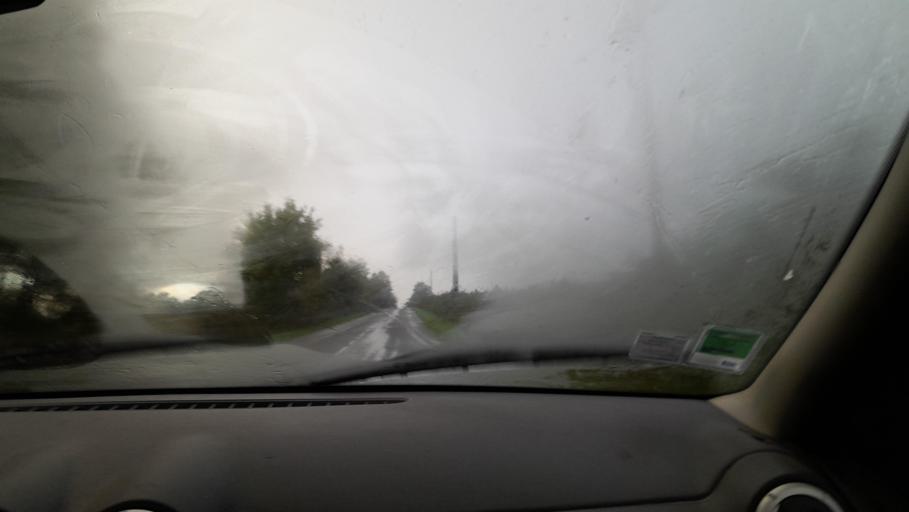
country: FR
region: Pays de la Loire
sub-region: Departement de la Mayenne
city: Ballots
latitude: 47.8677
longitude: -1.0479
